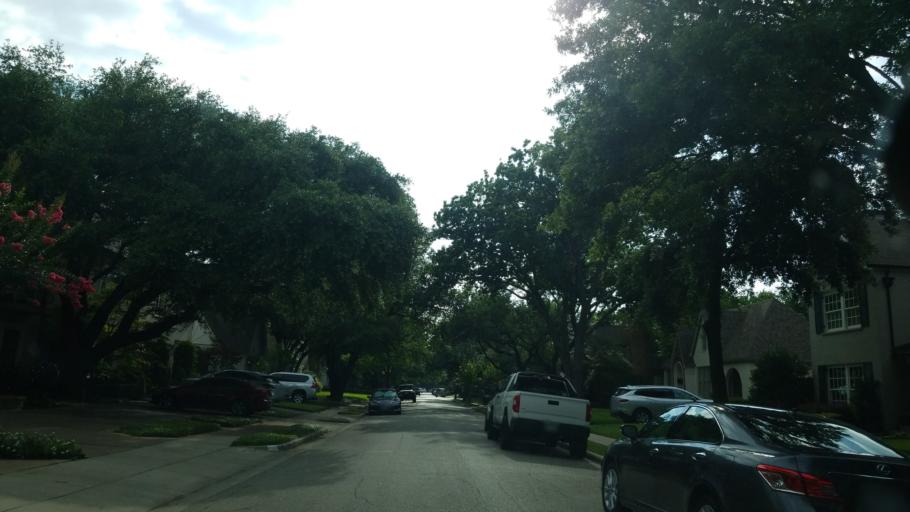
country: US
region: Texas
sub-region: Dallas County
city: University Park
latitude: 32.8413
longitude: -96.8055
